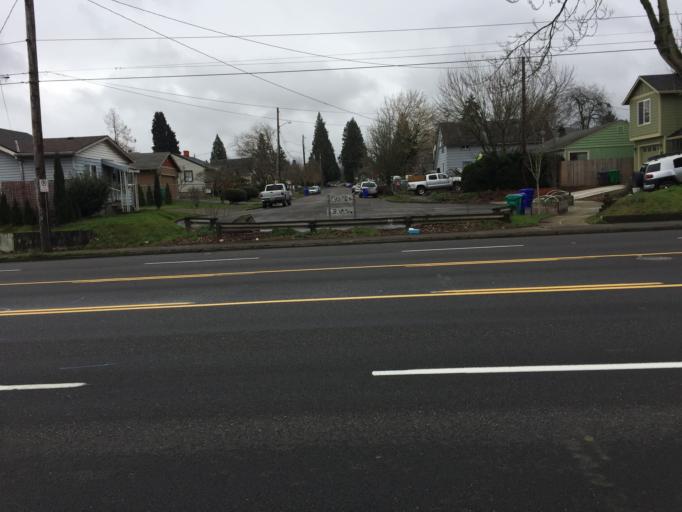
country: US
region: Washington
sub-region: Clark County
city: Vancouver
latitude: 45.5944
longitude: -122.7221
